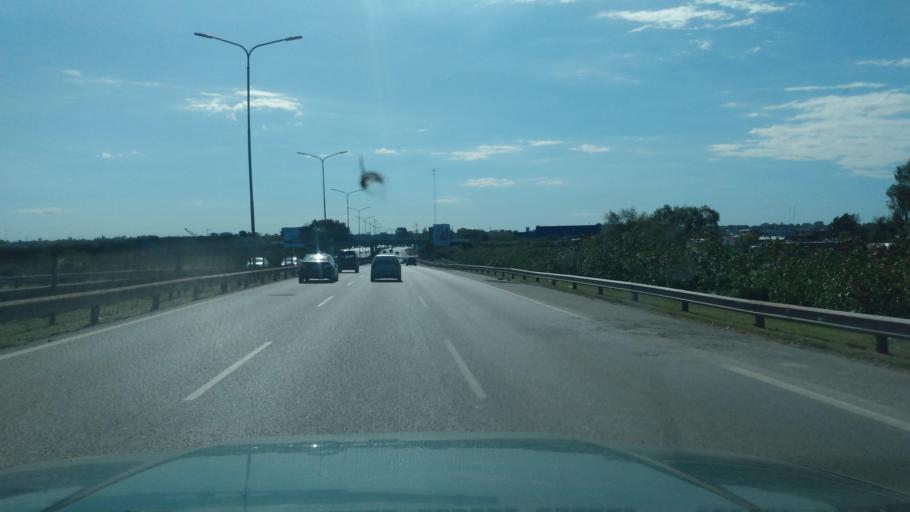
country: AR
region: Buenos Aires
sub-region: Partido de Tigre
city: Tigre
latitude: -34.5083
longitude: -58.5895
